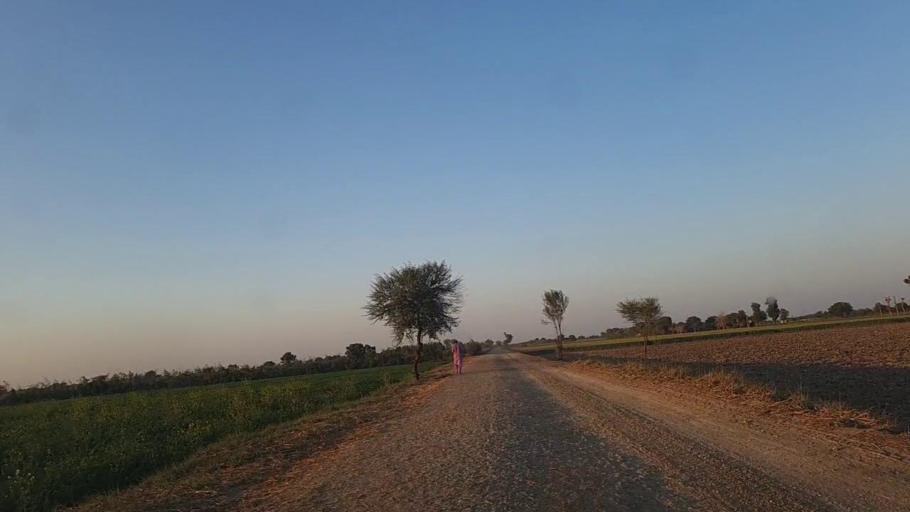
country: PK
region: Sindh
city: Naukot
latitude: 25.0405
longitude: 69.4099
